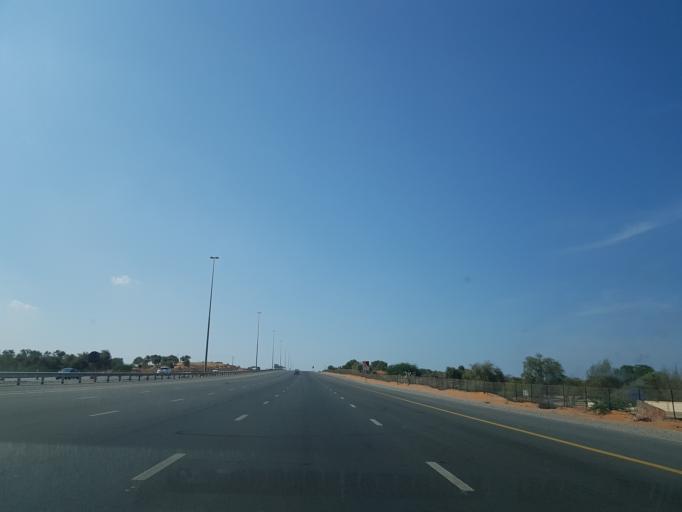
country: AE
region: Ra's al Khaymah
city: Ras al-Khaimah
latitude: 25.7025
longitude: 55.9596
